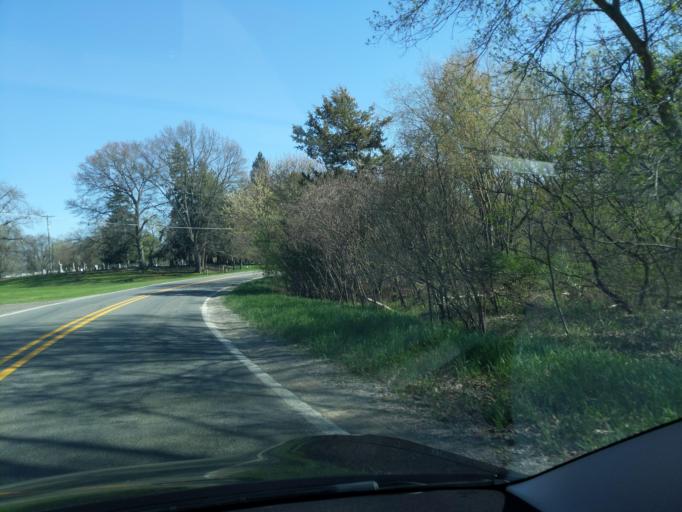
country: US
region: Michigan
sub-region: Ingham County
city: Stockbridge
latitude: 42.4421
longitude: -84.0973
